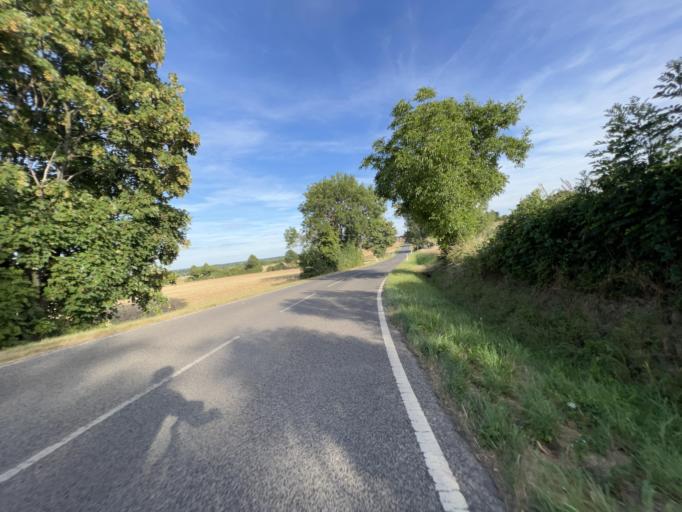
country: DE
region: North Rhine-Westphalia
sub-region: Regierungsbezirk Koln
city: Kreuzau
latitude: 50.7663
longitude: 6.4534
